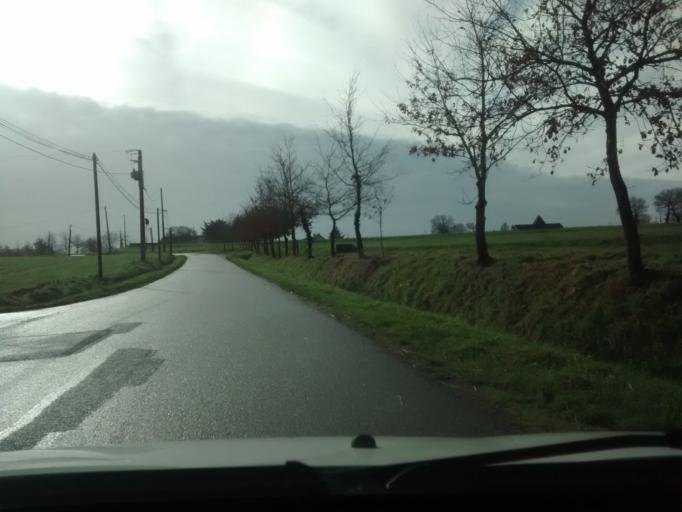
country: FR
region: Brittany
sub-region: Departement d'Ille-et-Vilaine
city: Pace
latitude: 48.1428
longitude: -1.7574
